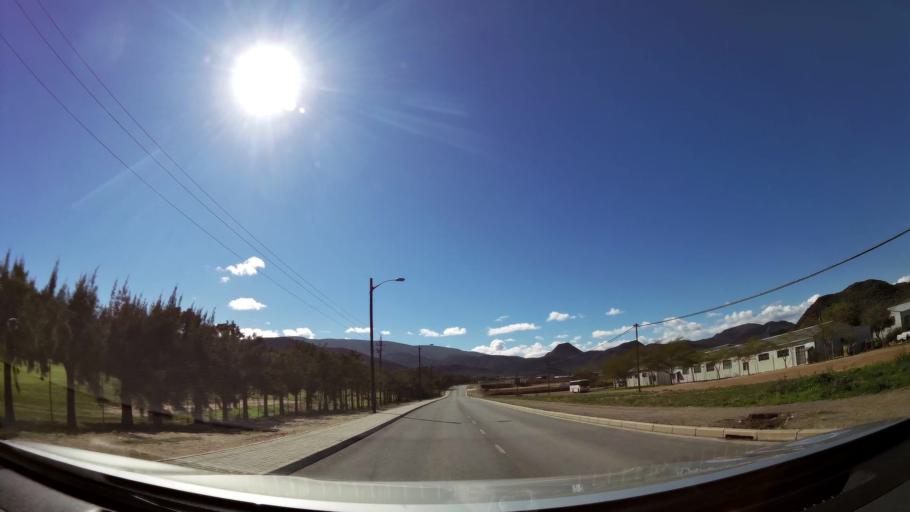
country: ZA
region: Western Cape
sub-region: Cape Winelands District Municipality
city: Ashton
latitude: -33.7745
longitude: 20.1342
